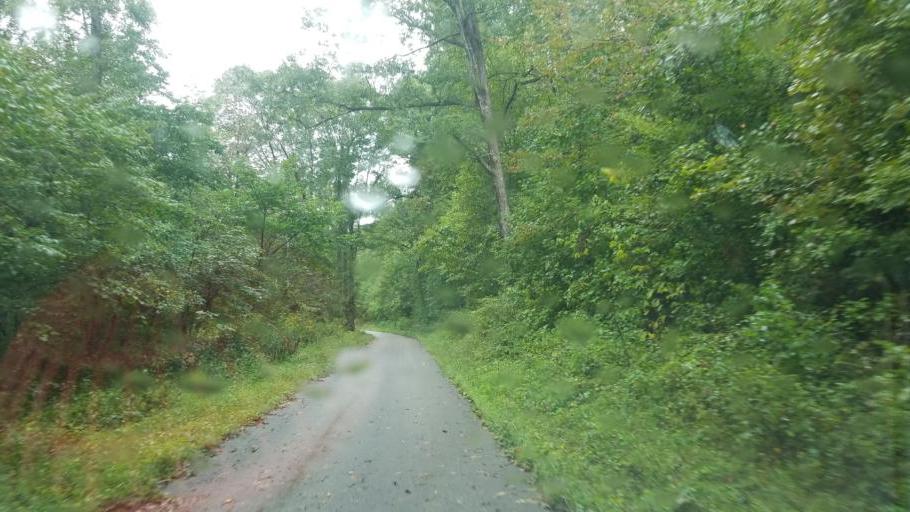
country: US
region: Ohio
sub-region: Scioto County
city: West Portsmouth
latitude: 38.7755
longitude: -83.1418
